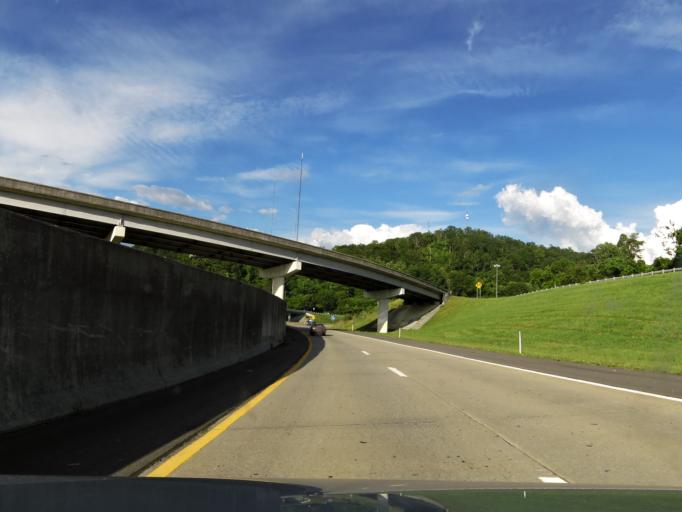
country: US
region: Tennessee
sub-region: Knox County
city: Knoxville
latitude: 35.9986
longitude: -83.9587
